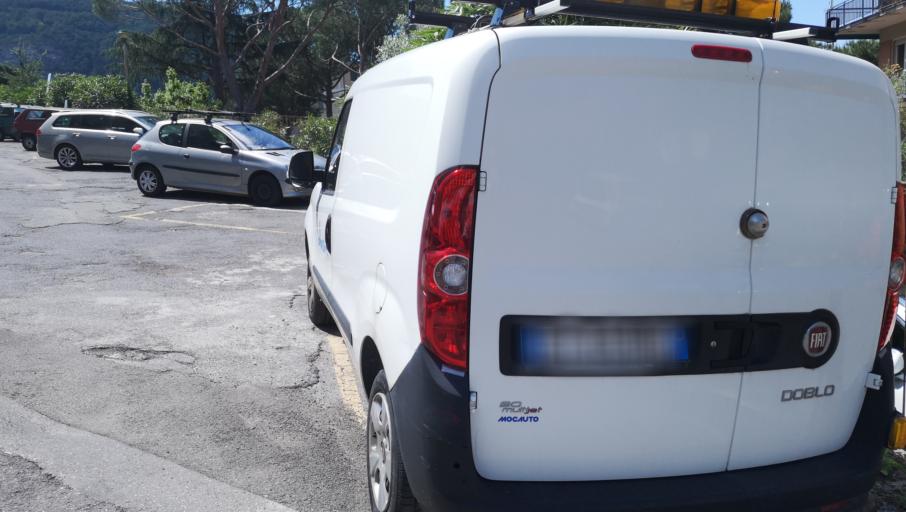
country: IT
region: Liguria
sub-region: Provincia di Genova
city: Piccarello
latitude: 44.4587
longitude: 8.9815
